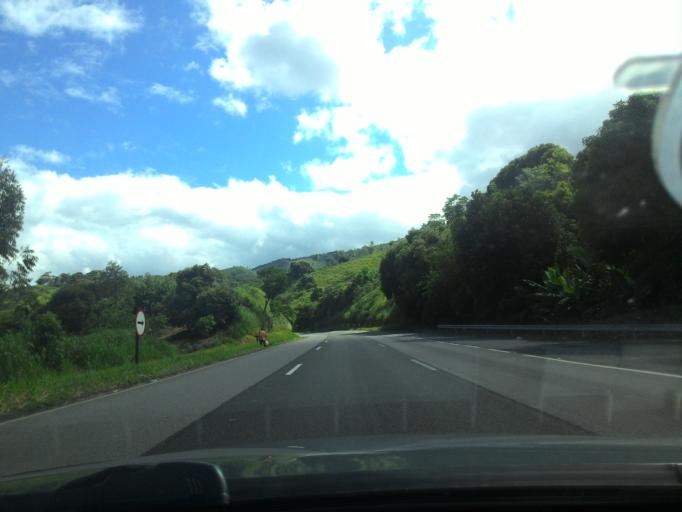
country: BR
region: Sao Paulo
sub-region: Cajati
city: Cajati
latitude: -24.8049
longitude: -48.2146
